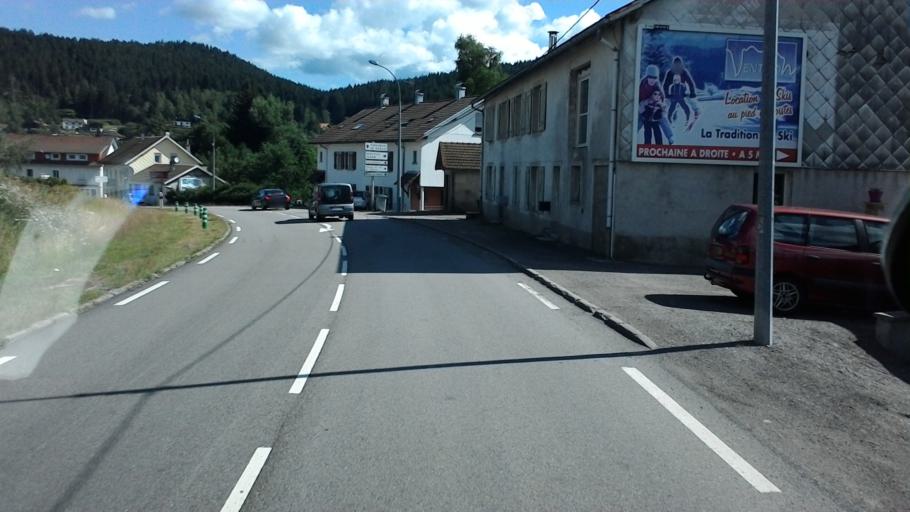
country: FR
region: Lorraine
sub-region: Departement des Vosges
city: Cornimont
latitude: 47.9432
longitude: 6.8322
